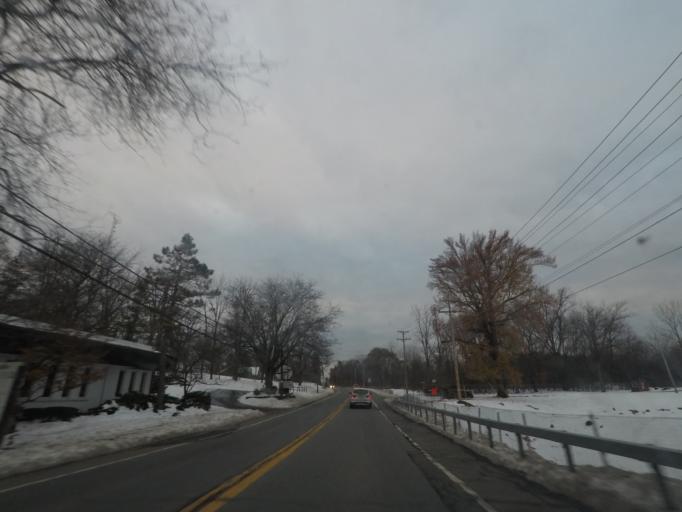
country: US
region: New York
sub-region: Orange County
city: Vails Gate
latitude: 41.4913
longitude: -74.0606
